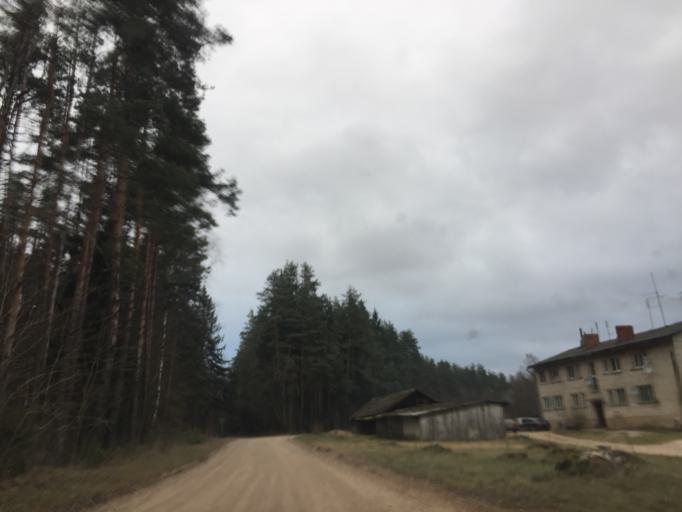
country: LV
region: Cesu Rajons
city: Cesis
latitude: 57.3543
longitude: 25.2605
